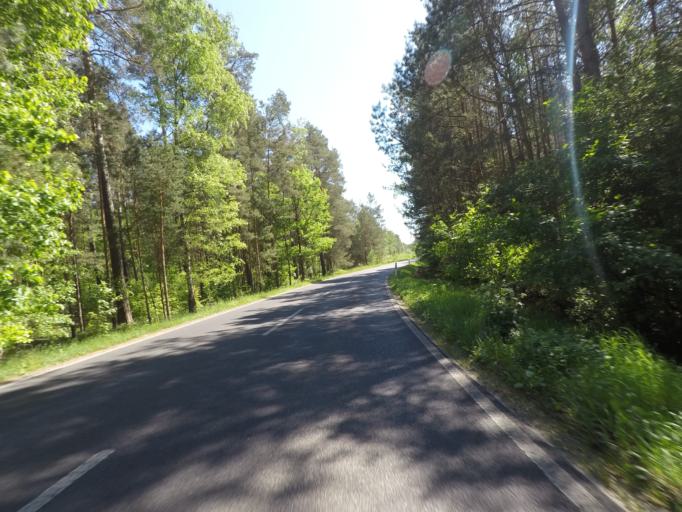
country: DE
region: Brandenburg
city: Eberswalde
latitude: 52.8261
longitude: 13.7702
